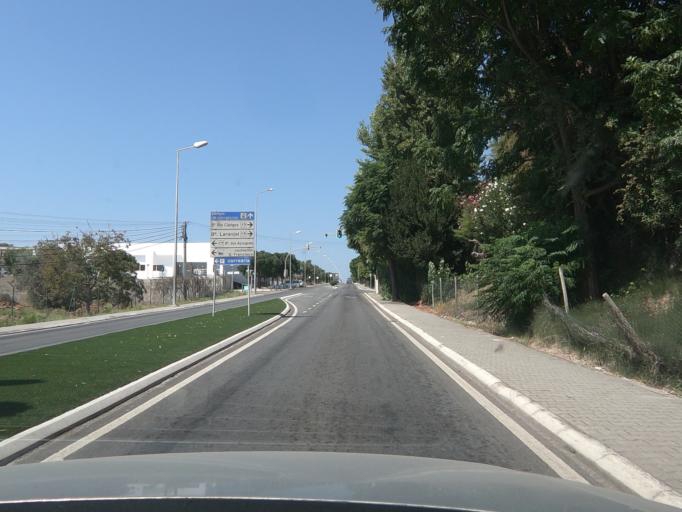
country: PT
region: Setubal
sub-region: Alcacer do Sal
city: Alcacer do Sal
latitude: 38.3748
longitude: -8.5093
